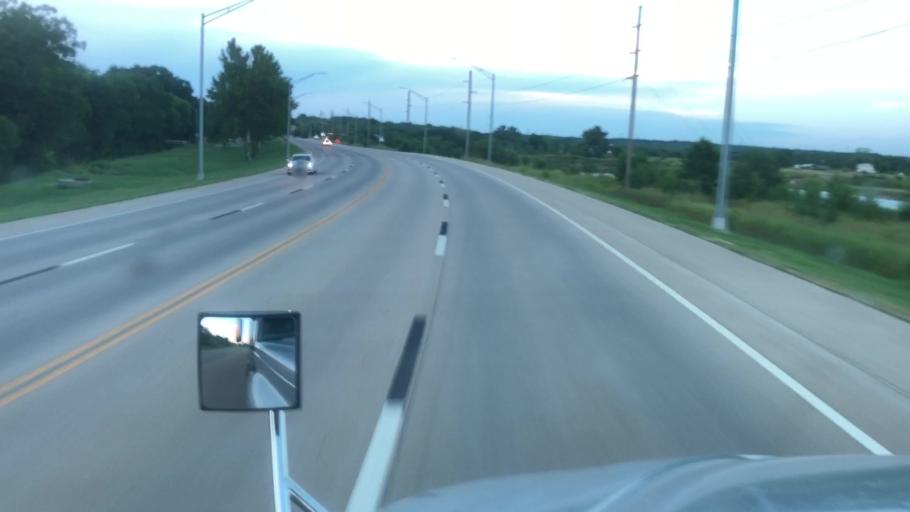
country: US
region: Oklahoma
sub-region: Kay County
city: Ponca City
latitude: 36.6894
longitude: -97.0671
